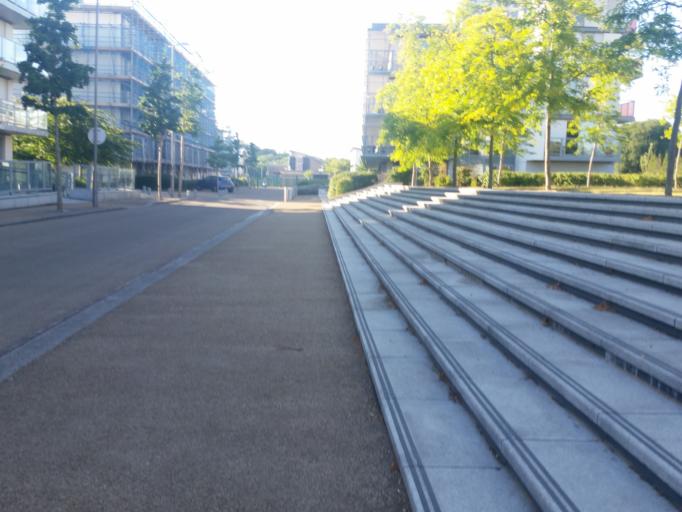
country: GB
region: England
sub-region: Greater London
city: Wood Green
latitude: 51.5906
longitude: -0.1158
